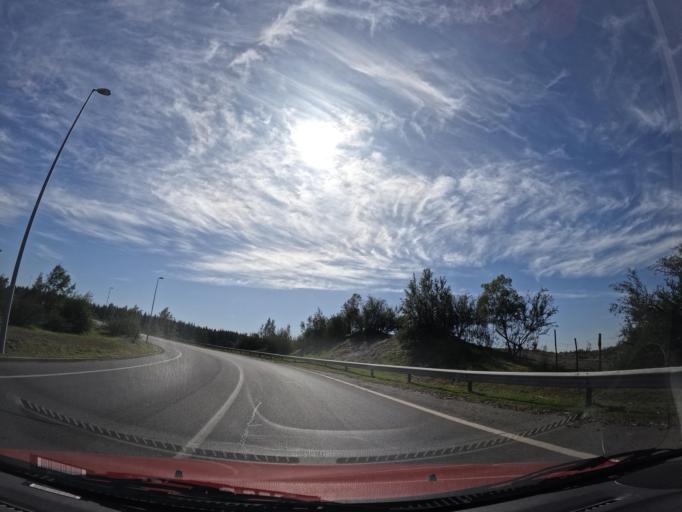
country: CL
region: Biobio
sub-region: Provincia de Biobio
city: Cabrero
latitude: -36.9340
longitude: -72.3446
